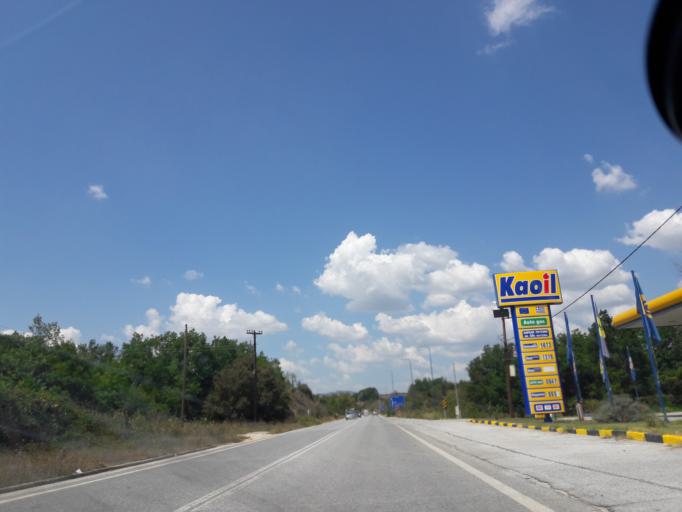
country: GR
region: Central Macedonia
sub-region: Nomos Chalkidikis
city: Galatista
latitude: 40.4628
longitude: 23.3743
